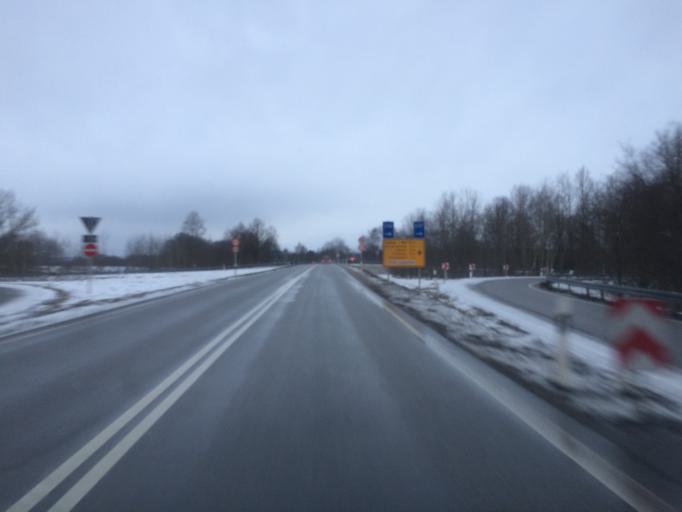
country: DE
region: Bavaria
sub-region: Upper Palatinate
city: Schwandorf in Bayern
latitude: 49.3448
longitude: 12.1440
